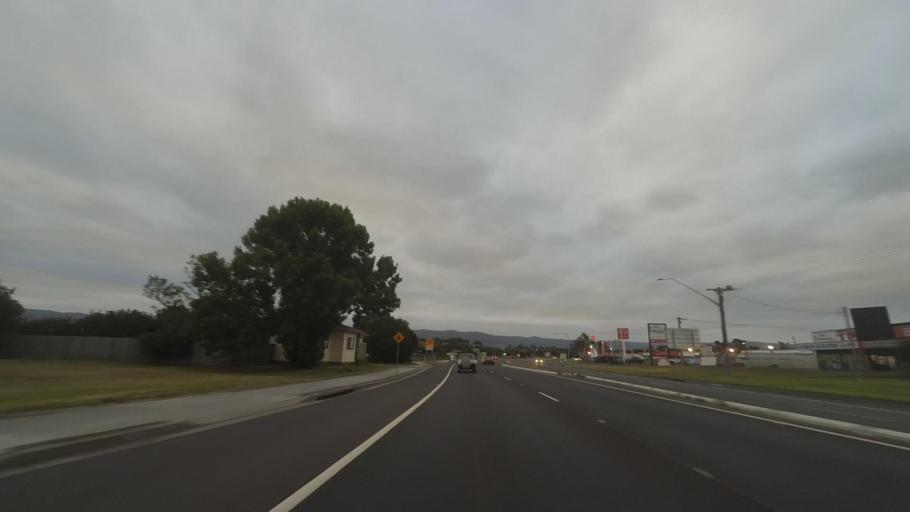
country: AU
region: New South Wales
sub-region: Shellharbour
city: Albion Park Rail
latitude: -34.5511
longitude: 150.7869
